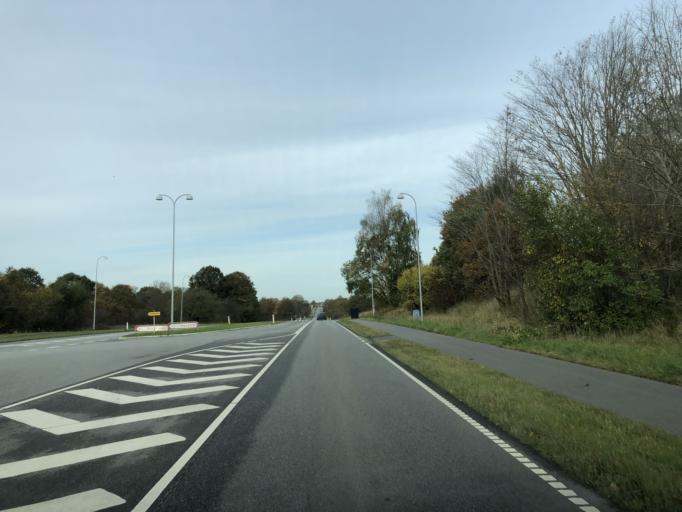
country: DK
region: Capital Region
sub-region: Allerod Kommune
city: Blovstrod
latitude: 55.8577
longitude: 12.4038
